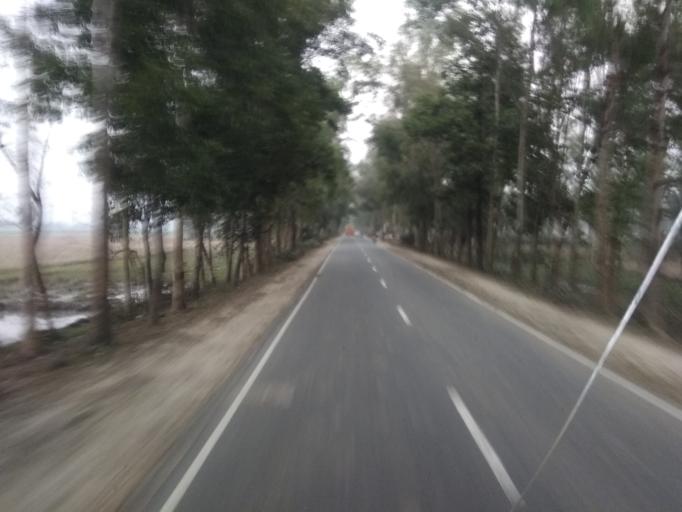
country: BD
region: Rajshahi
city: Bogra
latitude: 24.6821
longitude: 89.2884
